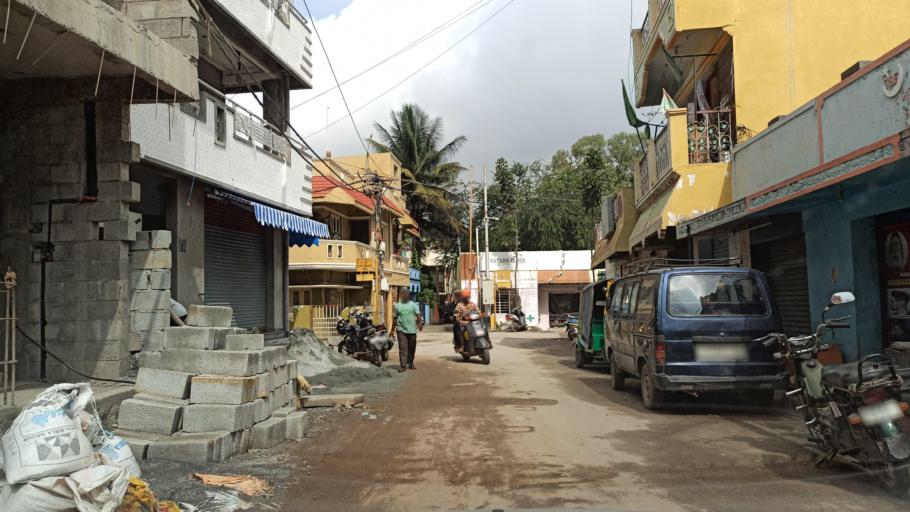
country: IN
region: Karnataka
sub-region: Bangalore Urban
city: Bangalore
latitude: 13.0029
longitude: 77.6715
